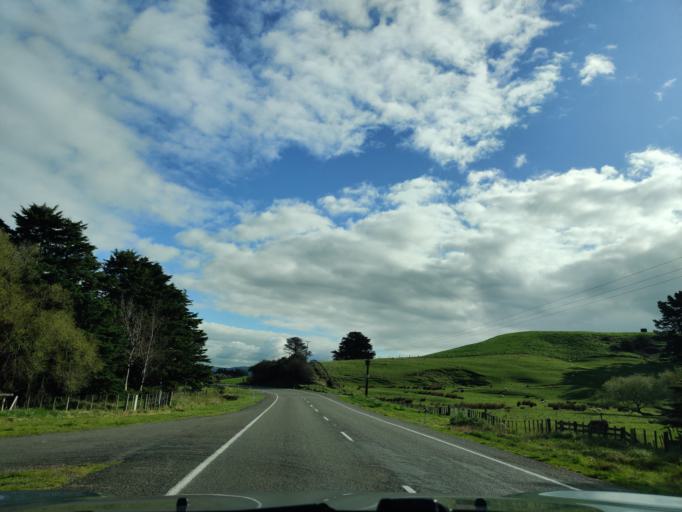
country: NZ
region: Manawatu-Wanganui
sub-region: Palmerston North City
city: Palmerston North
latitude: -40.3387
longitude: 175.8909
